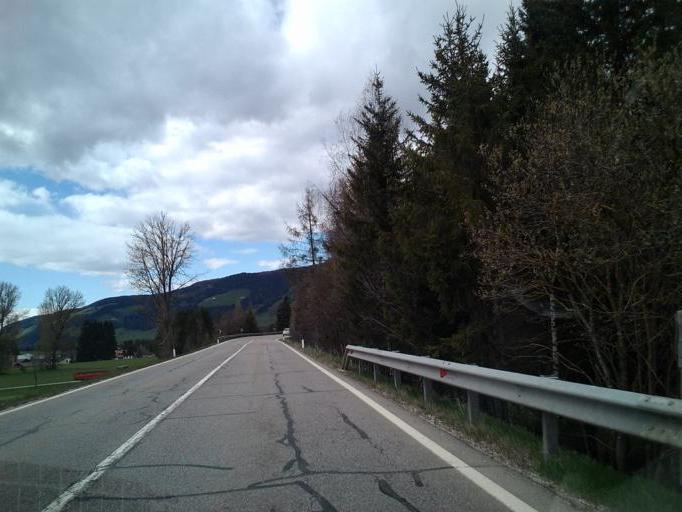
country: IT
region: Trentino-Alto Adige
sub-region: Bolzano
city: Dobbiaco
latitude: 46.7230
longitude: 12.2227
